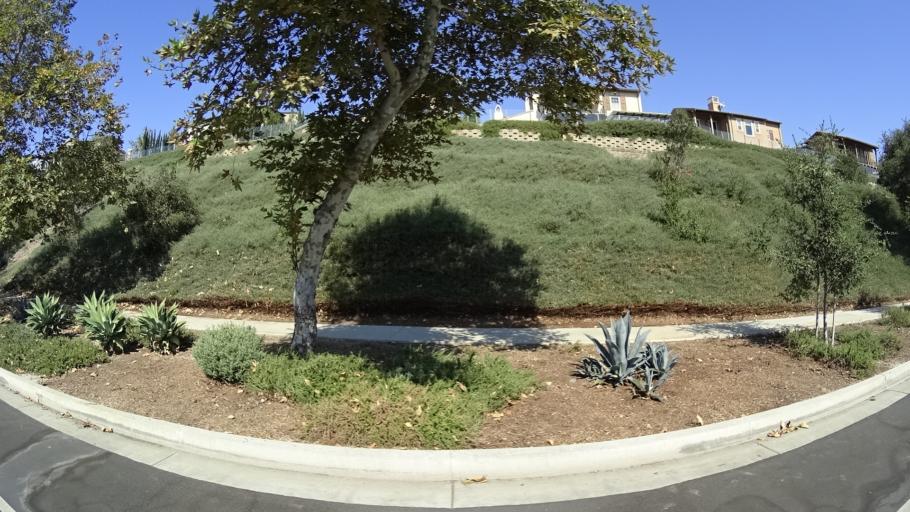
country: US
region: California
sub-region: Orange County
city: San Clemente
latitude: 33.4774
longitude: -117.5876
